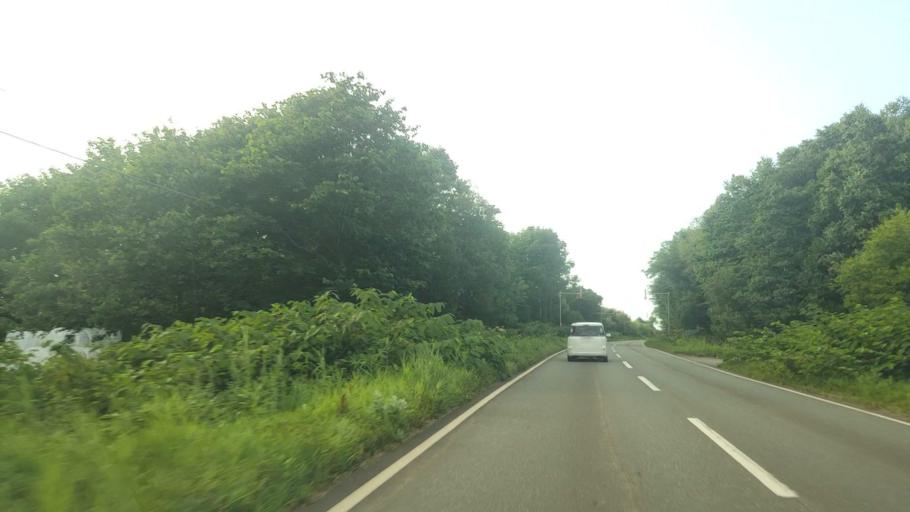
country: JP
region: Hokkaido
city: Makubetsu
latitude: 45.0467
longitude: 141.7527
